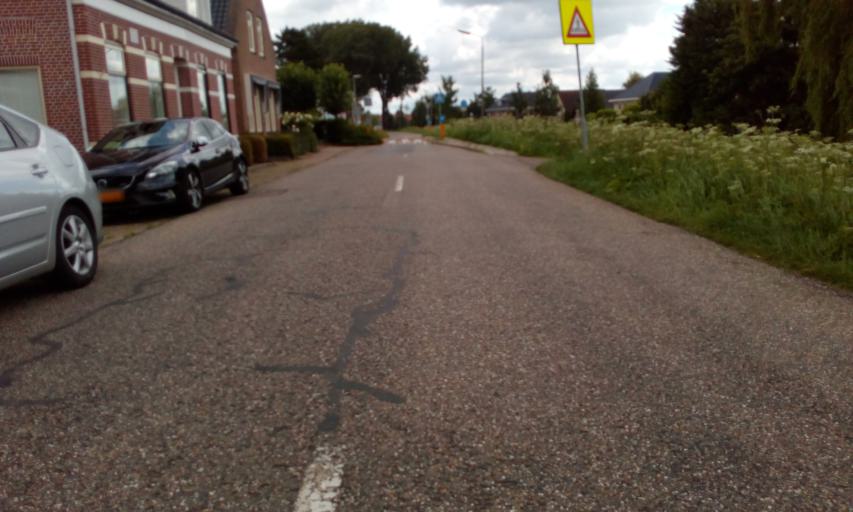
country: NL
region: South Holland
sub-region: Gemeente Binnenmaas
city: Heinenoord
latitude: 51.8588
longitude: 4.4840
